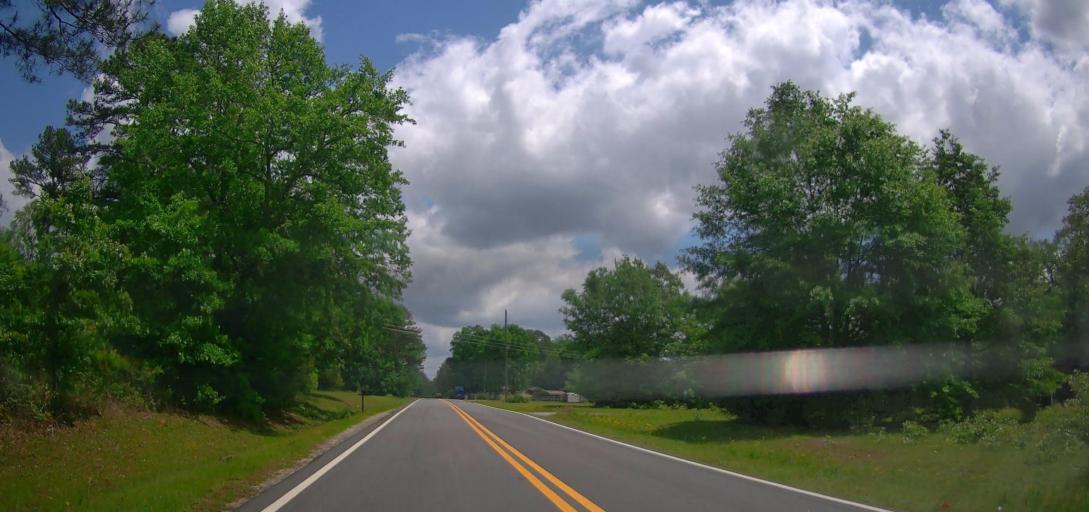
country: US
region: Georgia
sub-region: Laurens County
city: Dublin
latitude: 32.6034
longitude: -82.9379
